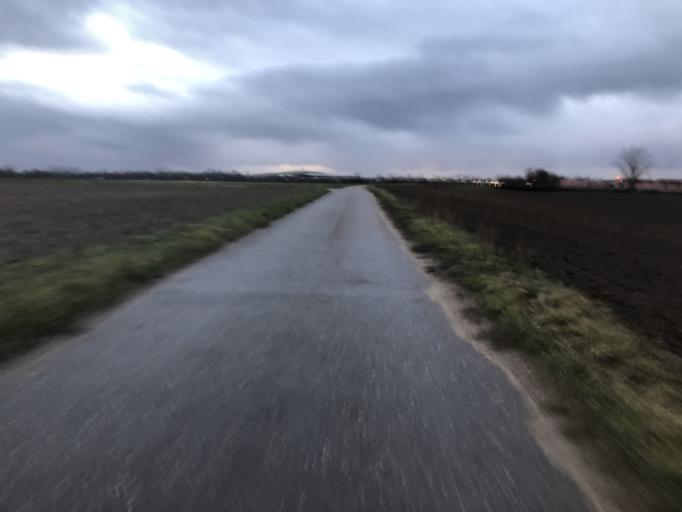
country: DE
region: Baden-Wuerttemberg
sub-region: Karlsruhe Region
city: Neulussheim
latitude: 49.3031
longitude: 8.5409
